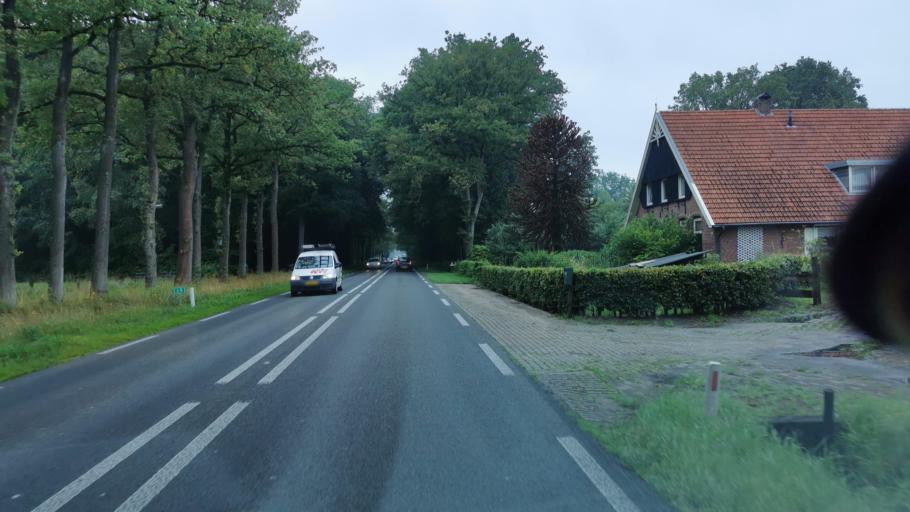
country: NL
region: Overijssel
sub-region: Gemeente Losser
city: Losser
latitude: 52.2762
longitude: 6.9765
